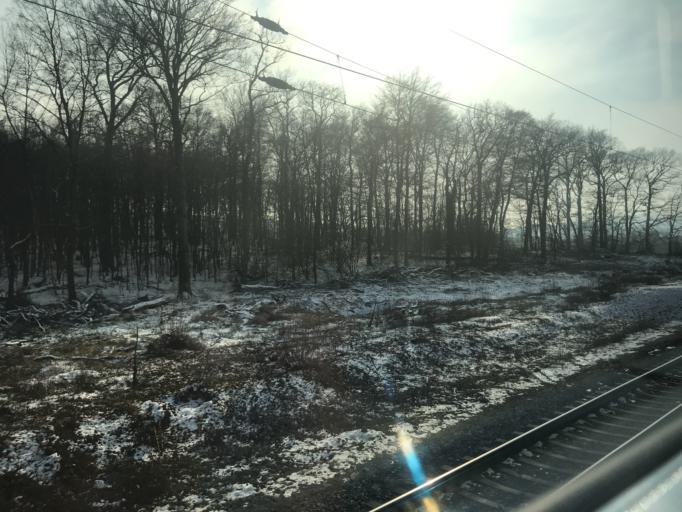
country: DE
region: Rheinland-Pfalz
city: Kinderbeuern
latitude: 49.9982
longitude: 7.0073
